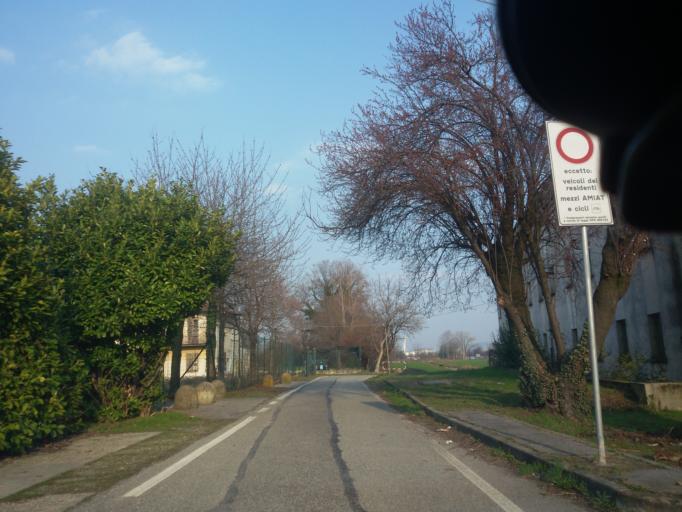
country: IT
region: Piedmont
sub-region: Provincia di Torino
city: Savonera
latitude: 45.1082
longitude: 7.6151
